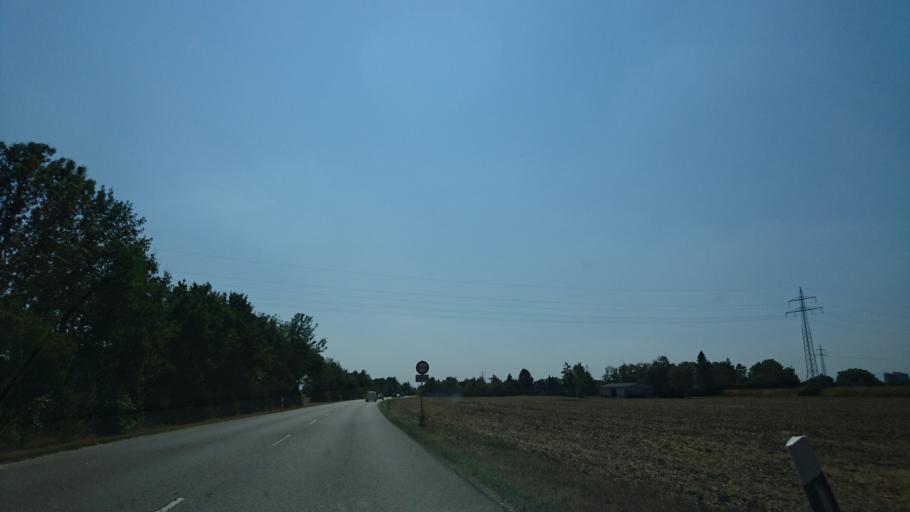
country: DE
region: Bavaria
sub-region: Swabia
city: Friedberg
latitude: 48.3486
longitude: 10.9655
